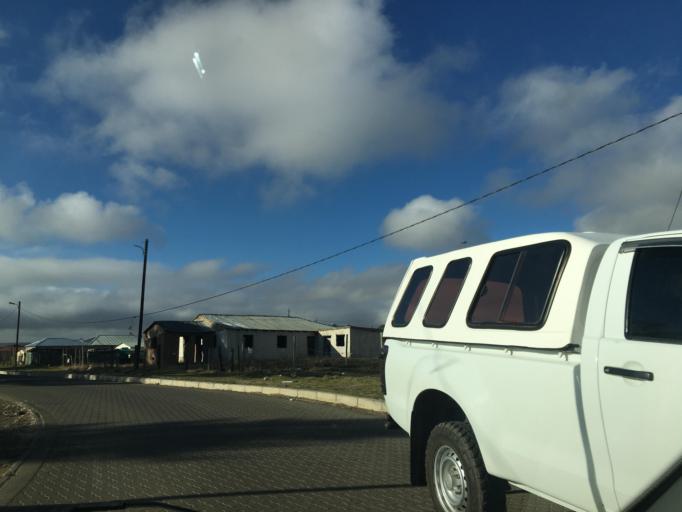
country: ZA
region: Eastern Cape
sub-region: Chris Hani District Municipality
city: Elliot
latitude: -31.3364
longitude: 27.8354
